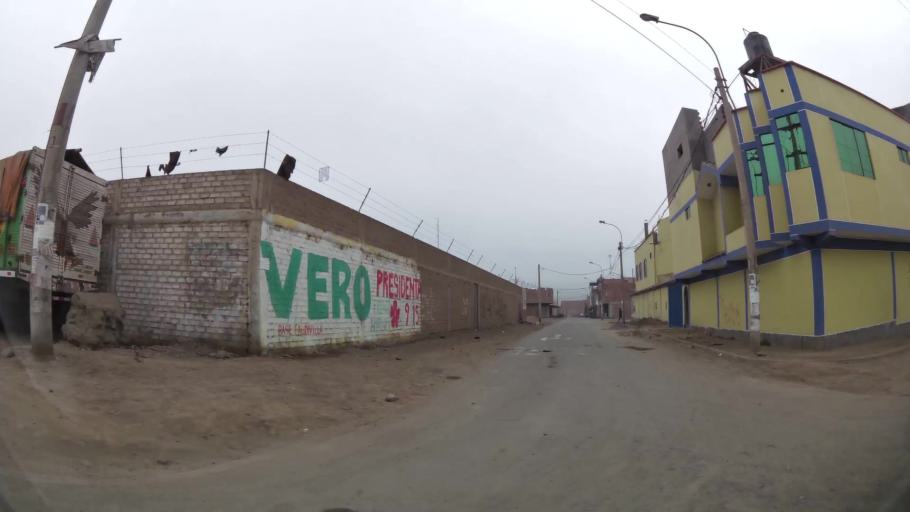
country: PE
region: Lima
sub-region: Lima
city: Urb. Santo Domingo
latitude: -11.8649
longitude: -77.0228
